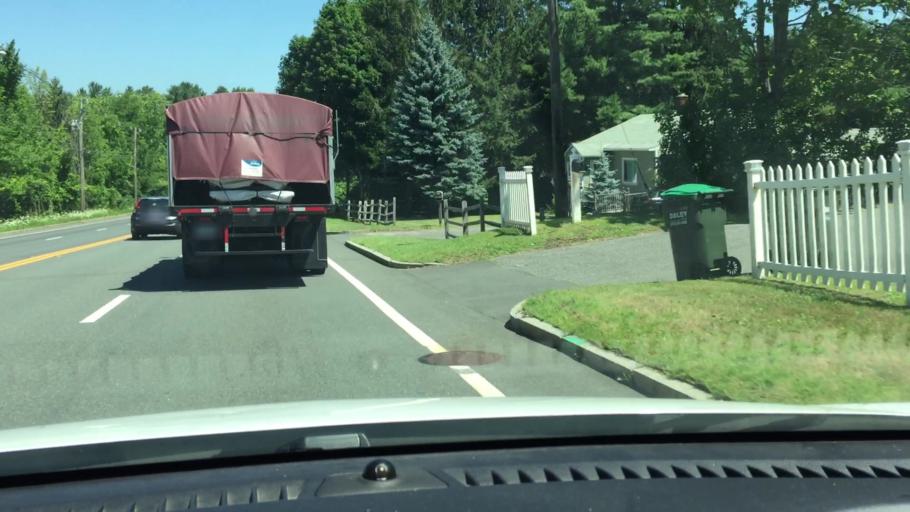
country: US
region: Massachusetts
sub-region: Berkshire County
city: Lenox
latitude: 42.3917
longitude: -73.2728
